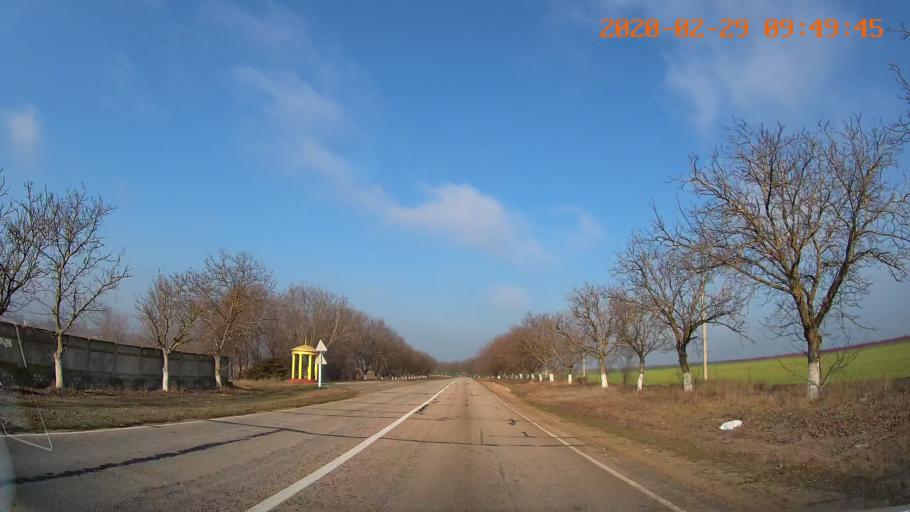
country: MD
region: Telenesti
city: Crasnoe
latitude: 46.6992
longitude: 29.7675
